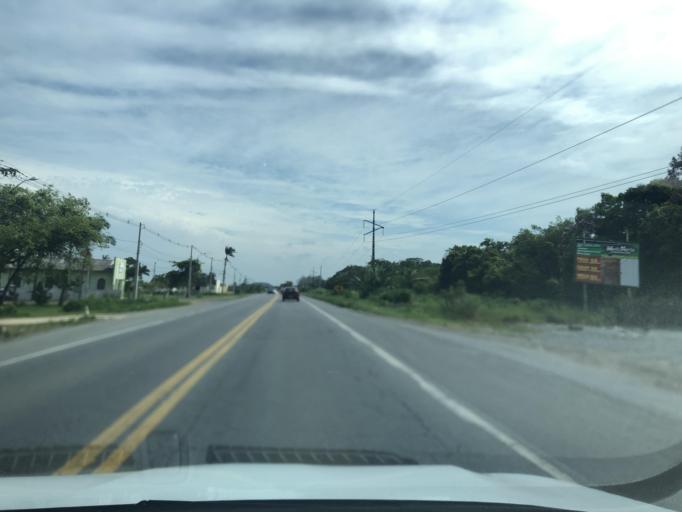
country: BR
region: Santa Catarina
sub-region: Sao Francisco Do Sul
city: Sao Francisco do Sul
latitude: -26.3366
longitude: -48.6541
